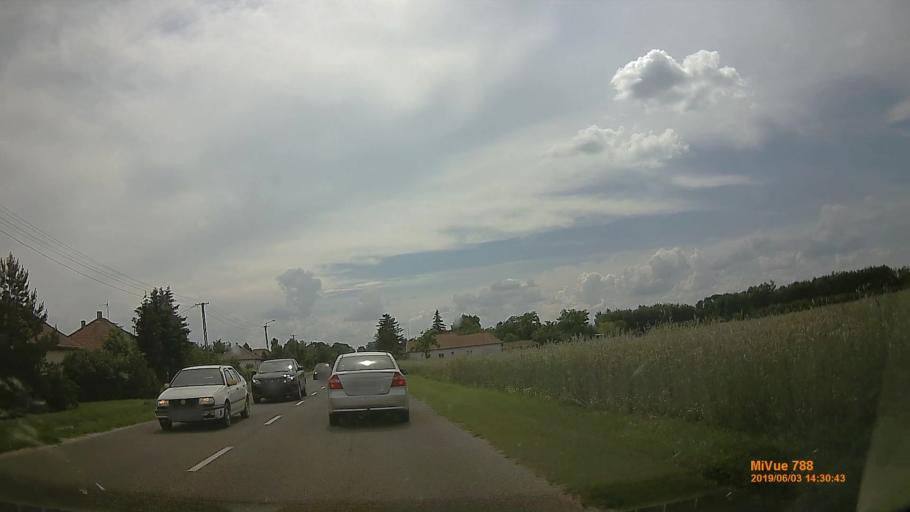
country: HU
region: Bacs-Kiskun
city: Tiszakecske
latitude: 46.9659
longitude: 20.1006
